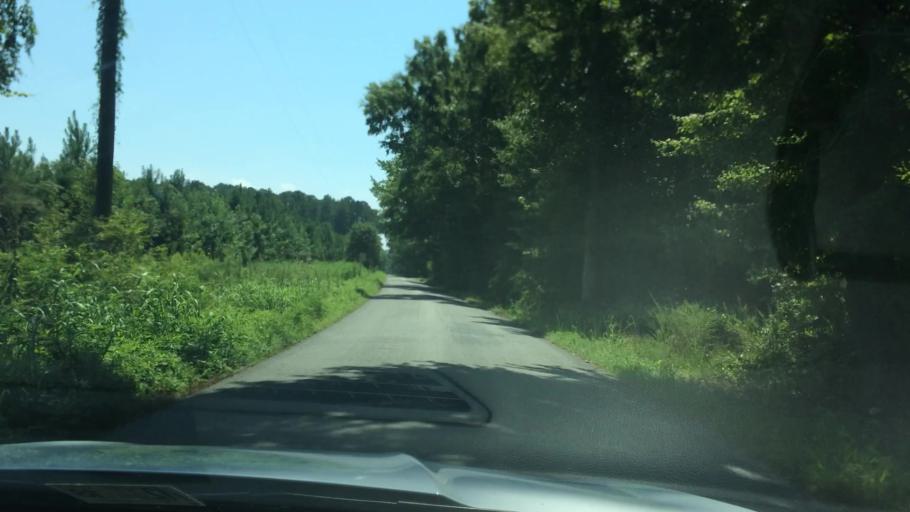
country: US
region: Virginia
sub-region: Charles City County
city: Charles City
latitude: 37.3025
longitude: -76.9657
